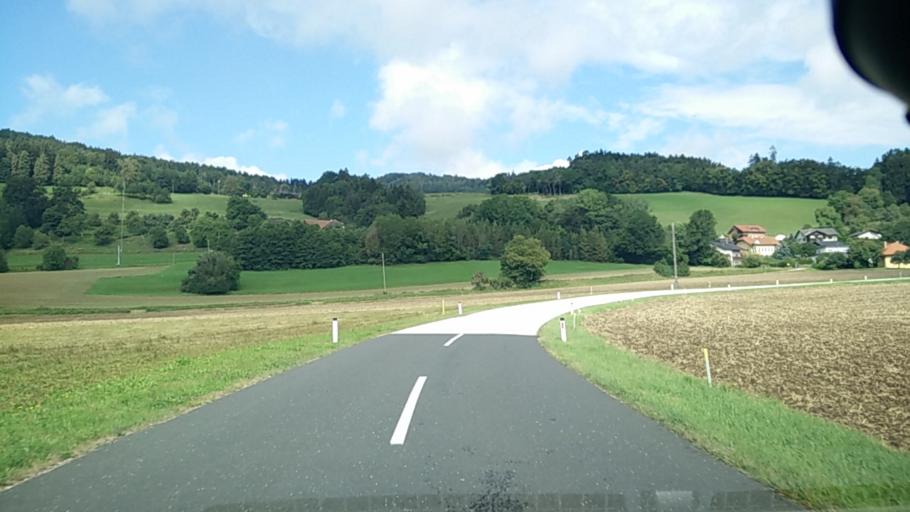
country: AT
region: Carinthia
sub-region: Politischer Bezirk Volkermarkt
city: Voelkermarkt
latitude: 46.6700
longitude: 14.5736
